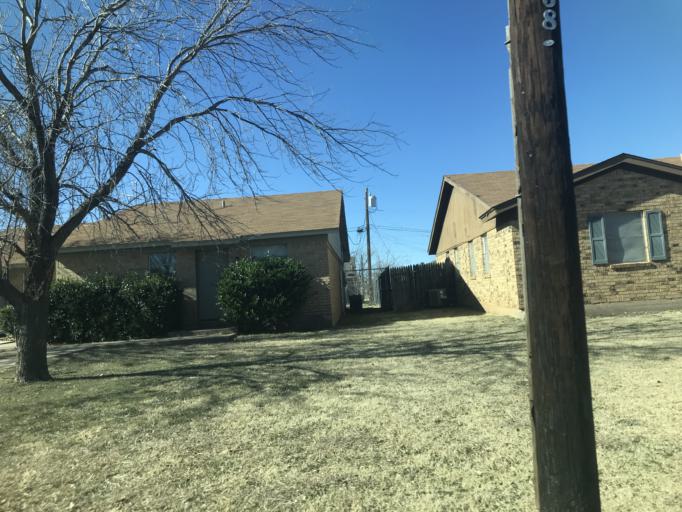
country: US
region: Texas
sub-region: Taylor County
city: Abilene
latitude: 32.4434
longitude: -99.8028
